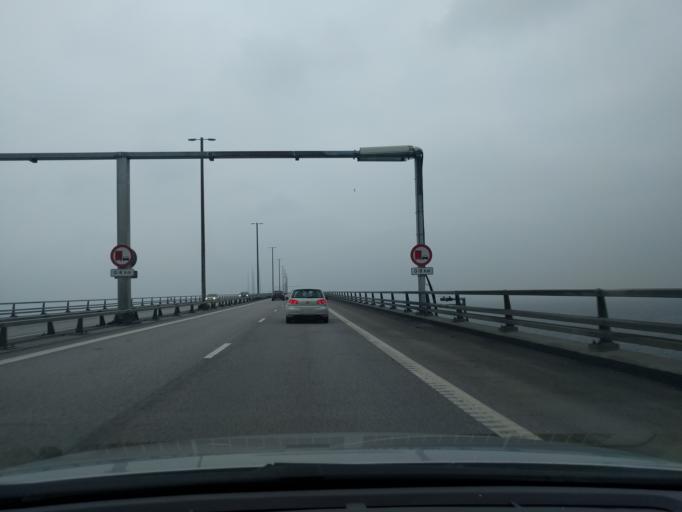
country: DK
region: Capital Region
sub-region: Dragor Kommune
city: Dragor
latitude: 55.5867
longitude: 12.7852
